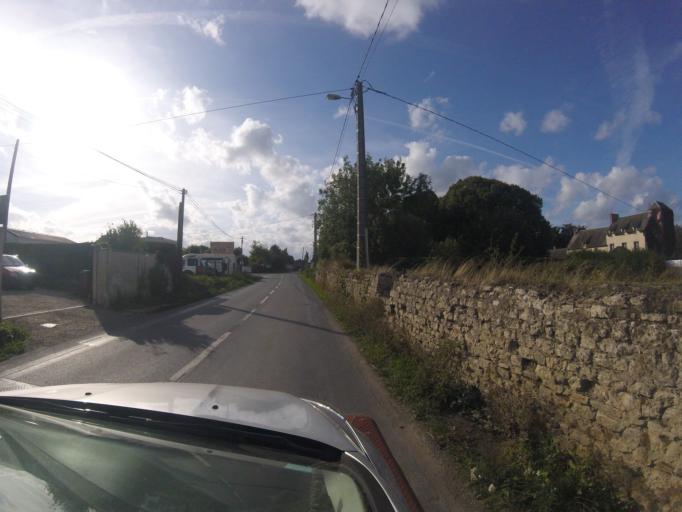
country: FR
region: Lower Normandy
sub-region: Departement du Calvados
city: Port-en-Bessin-Huppain
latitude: 49.3491
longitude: -0.8192
